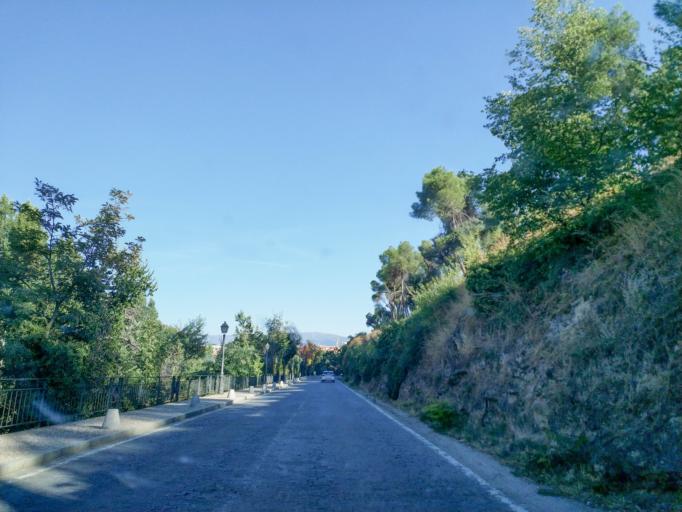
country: ES
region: Castille and Leon
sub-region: Provincia de Segovia
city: Segovia
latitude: 40.9485
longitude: -4.1270
